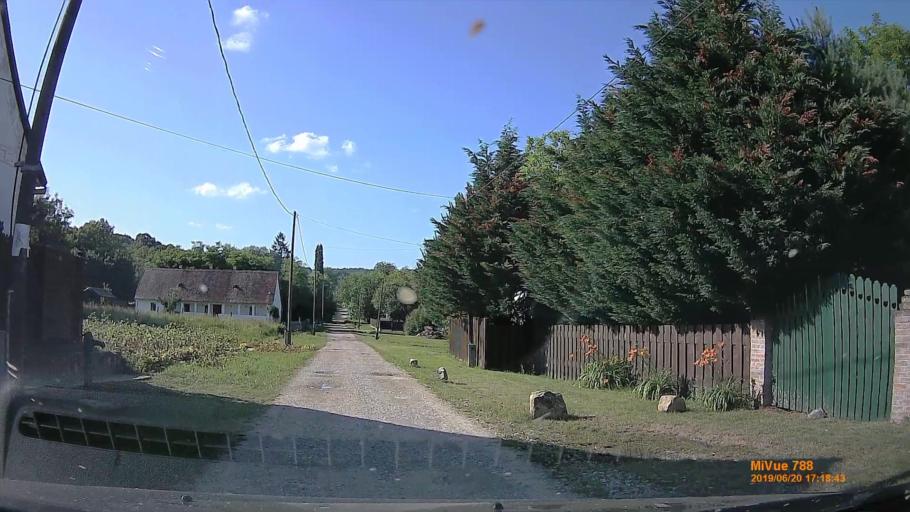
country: HU
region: Baranya
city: Buekkoesd
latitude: 46.1599
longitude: 18.0105
